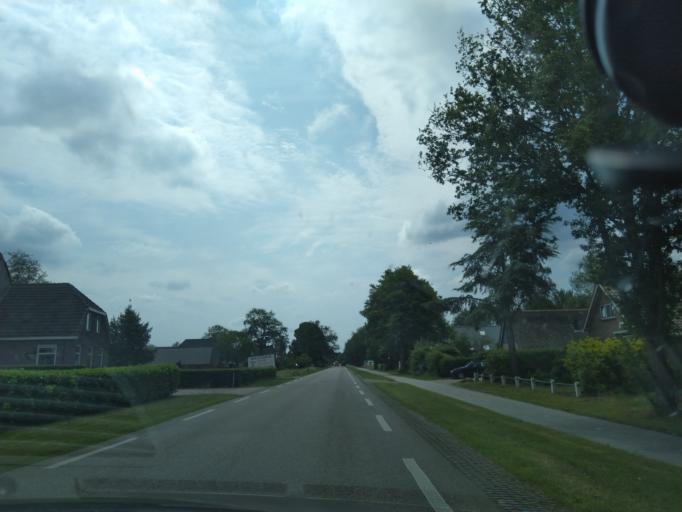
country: NL
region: Drenthe
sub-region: Gemeente Assen
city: Assen
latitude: 52.8882
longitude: 6.5312
